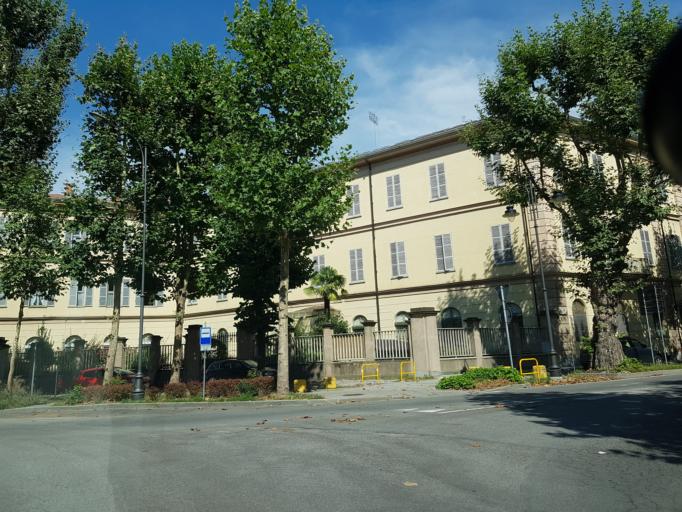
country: IT
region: Piedmont
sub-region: Provincia di Cuneo
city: Cuneo
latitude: 44.3878
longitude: 7.5490
